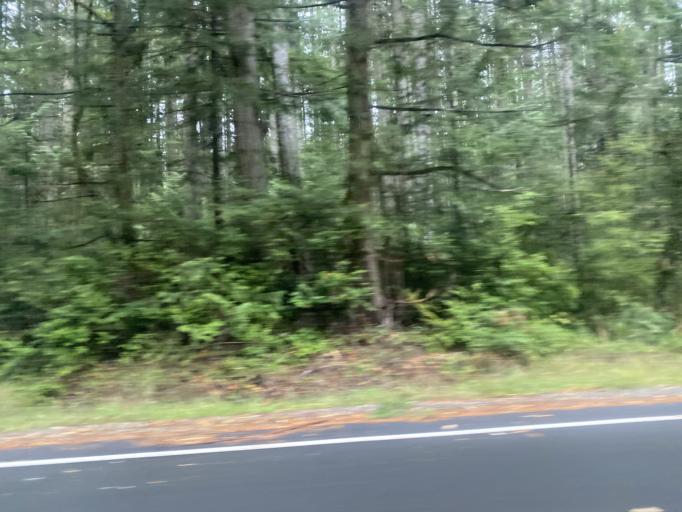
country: US
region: Washington
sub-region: Island County
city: Freeland
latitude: 48.0664
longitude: -122.4851
